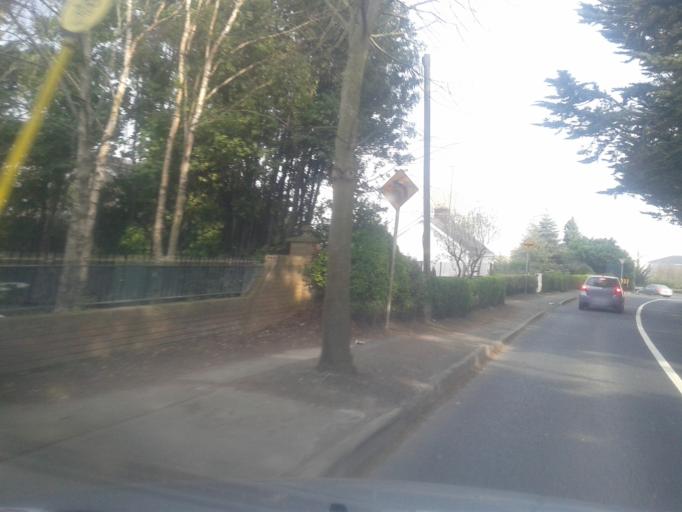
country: IE
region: Leinster
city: Kinsealy-Drinan
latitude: 53.4505
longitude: -6.2050
